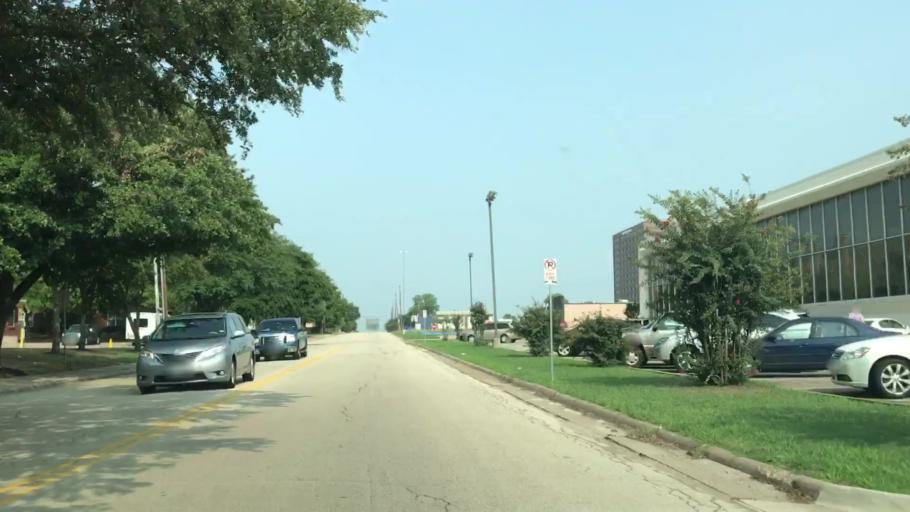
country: US
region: Texas
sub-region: Dallas County
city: Richardson
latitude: 32.9137
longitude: -96.7443
